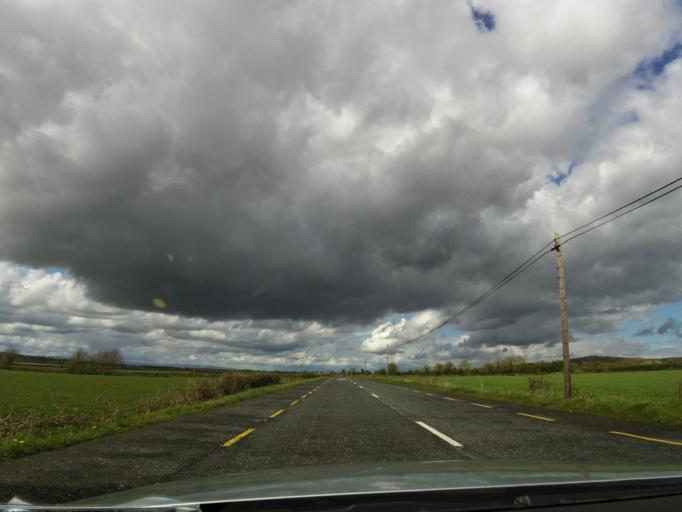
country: IE
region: Leinster
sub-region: Laois
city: Rathdowney
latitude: 52.7687
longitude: -7.5413
